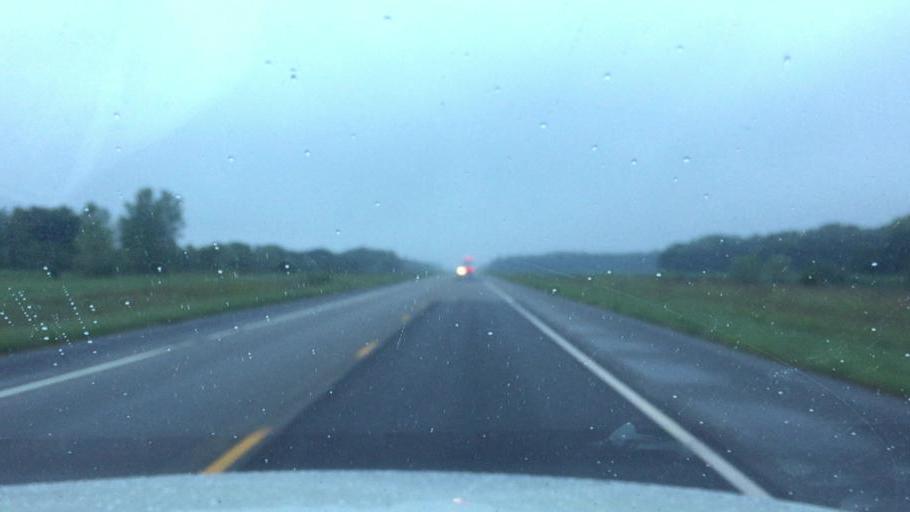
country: US
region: Kansas
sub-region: Montgomery County
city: Cherryvale
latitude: 37.4253
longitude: -95.4927
